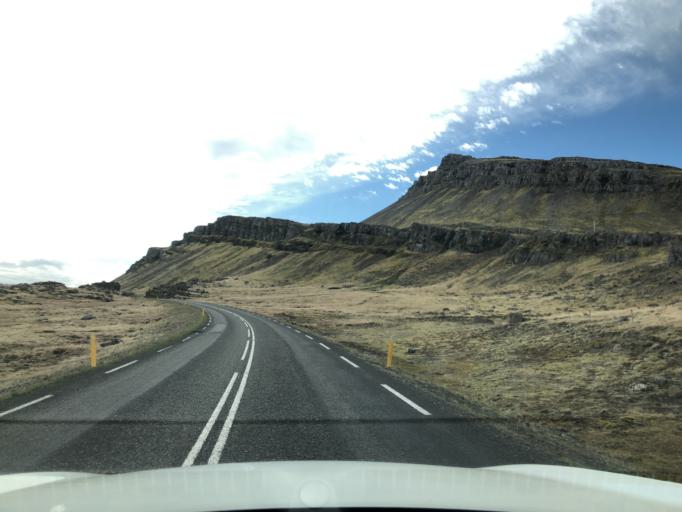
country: IS
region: East
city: Eskifjoerdur
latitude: 64.7459
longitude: -14.0113
